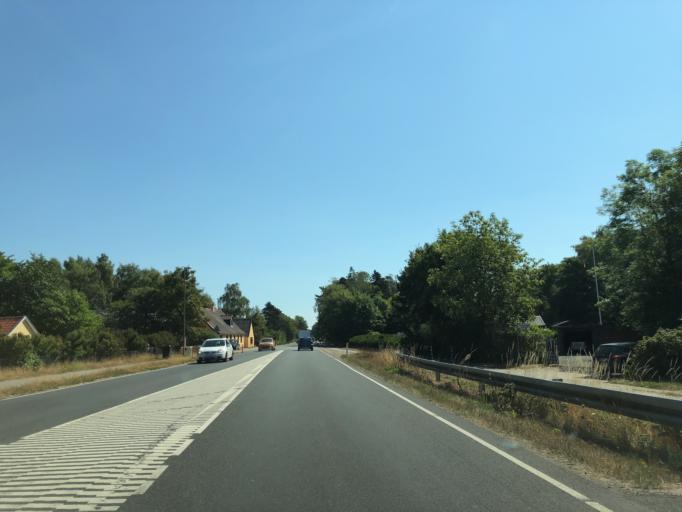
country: DK
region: Zealand
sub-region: Odsherred Kommune
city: Nykobing Sjaelland
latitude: 55.9379
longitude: 11.6860
